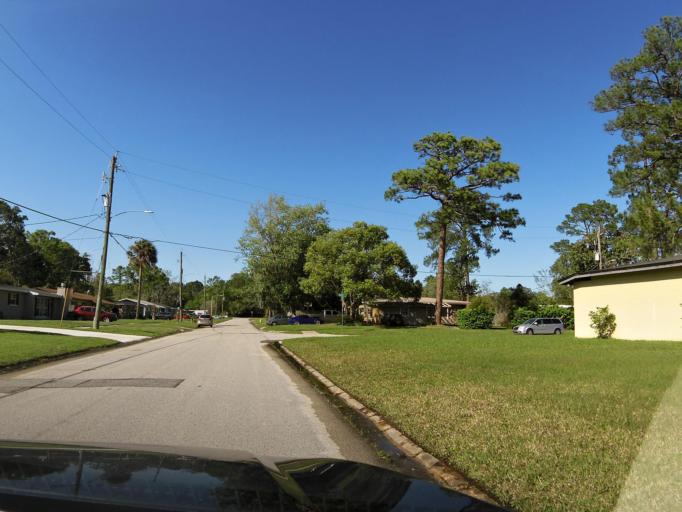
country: US
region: Florida
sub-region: Duval County
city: Jacksonville
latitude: 30.2813
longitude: -81.5993
